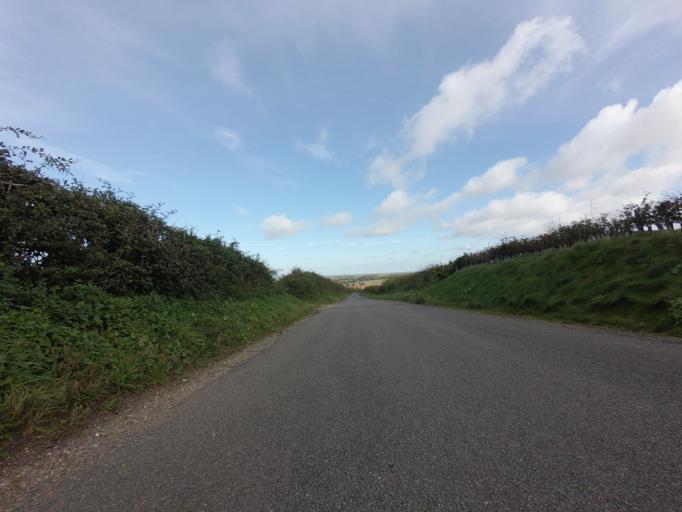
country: GB
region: England
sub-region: Norfolk
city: Wells-next-the-Sea
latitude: 52.9342
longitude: 0.7271
